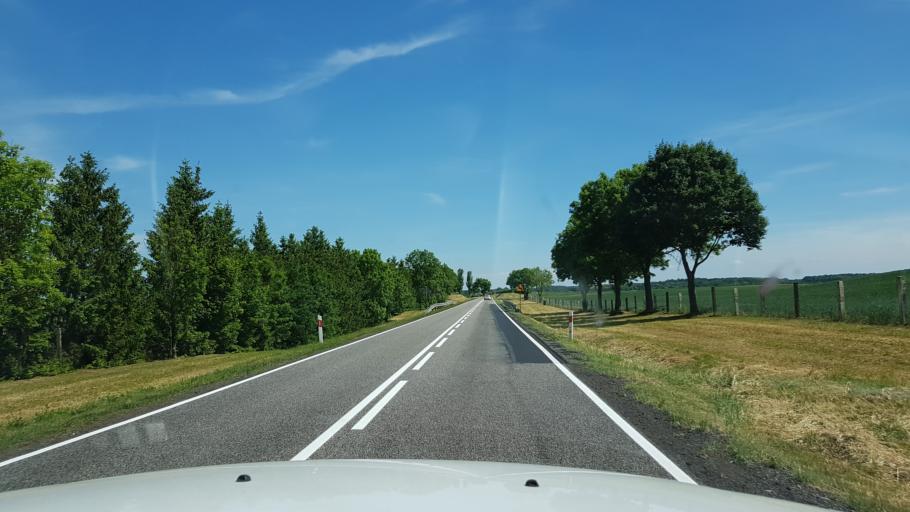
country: PL
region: West Pomeranian Voivodeship
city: Trzcinsko Zdroj
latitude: 52.9599
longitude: 14.5244
